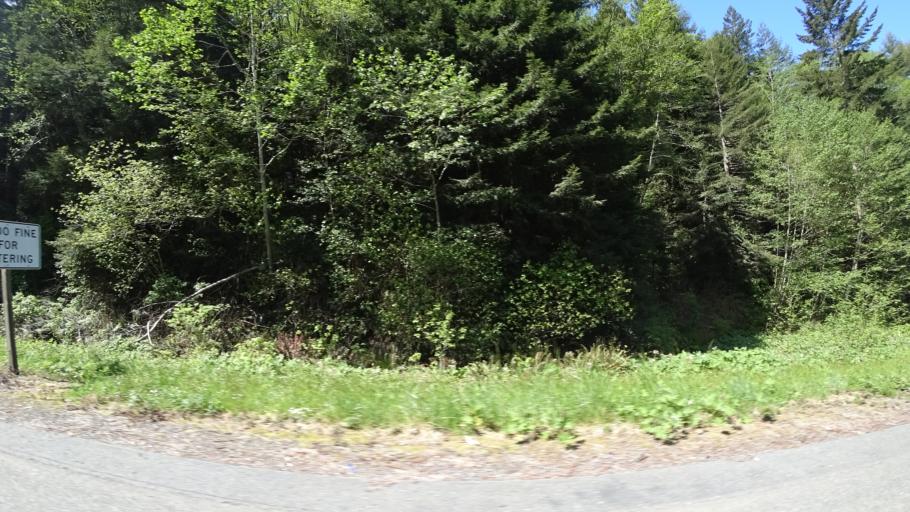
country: US
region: California
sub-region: Del Norte County
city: Bertsch-Oceanview
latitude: 41.4646
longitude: -124.0375
